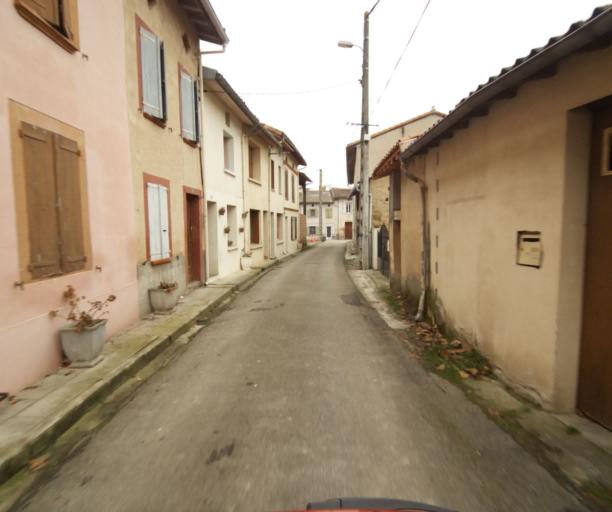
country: FR
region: Midi-Pyrenees
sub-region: Departement de la Haute-Garonne
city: Gaillac-Toulza
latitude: 43.2686
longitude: 1.5108
